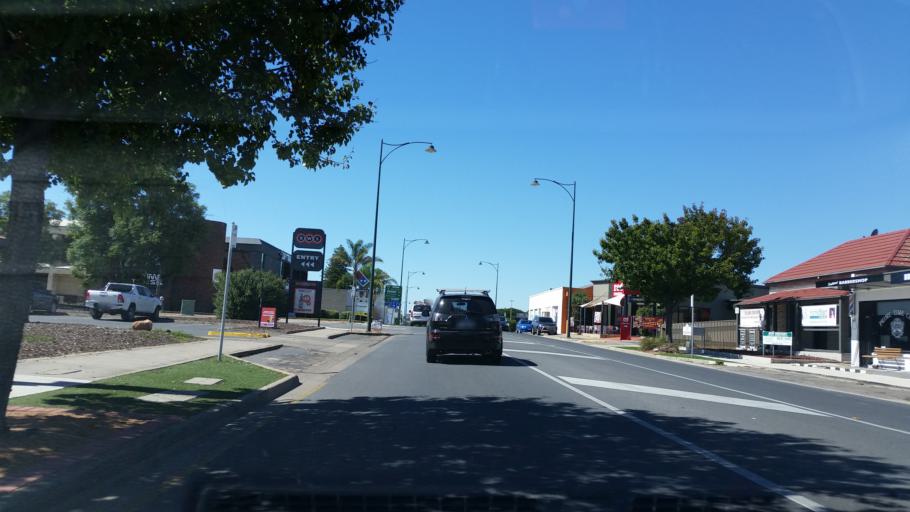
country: AU
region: South Australia
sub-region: Murray Bridge
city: Murray Bridge
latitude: -35.1210
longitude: 139.2714
